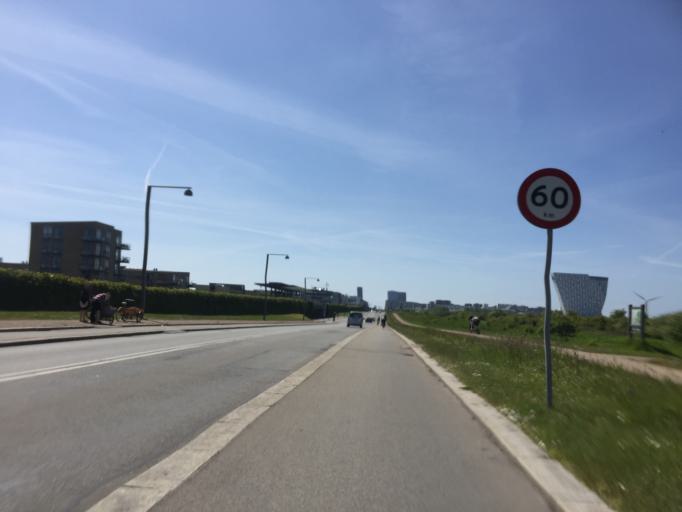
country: DK
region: Capital Region
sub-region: Tarnby Kommune
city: Tarnby
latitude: 55.6469
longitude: 12.5859
